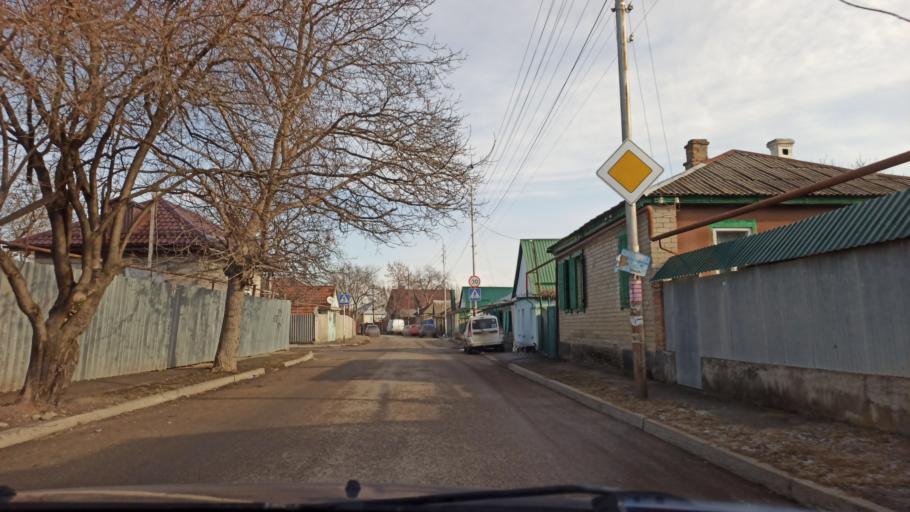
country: RU
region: Stavropol'skiy
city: Yessentuki
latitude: 44.0315
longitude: 42.8581
